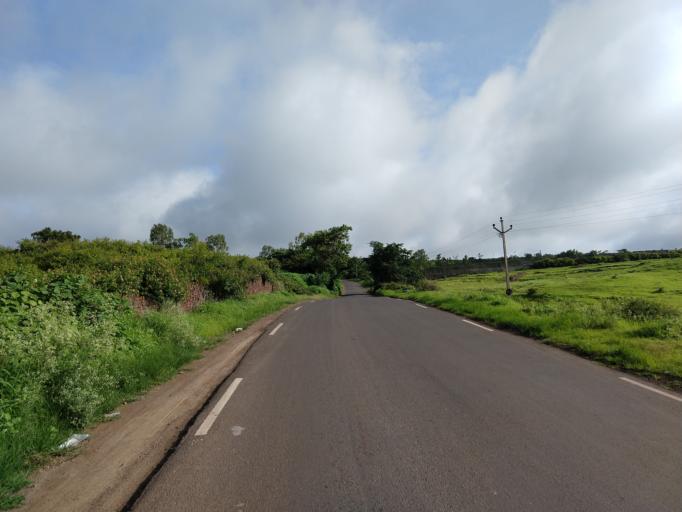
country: IN
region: Maharashtra
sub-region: Pune Division
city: Khed
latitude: 18.3996
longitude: 73.9126
